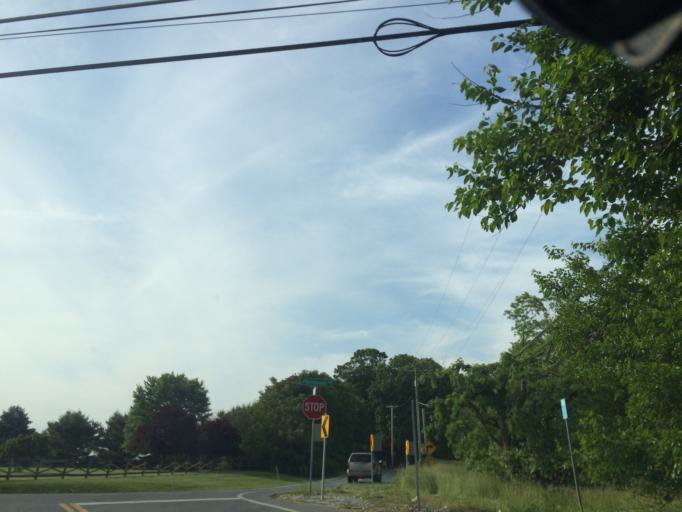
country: US
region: Maryland
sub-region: Carroll County
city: Sykesville
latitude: 39.2817
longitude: -77.0185
